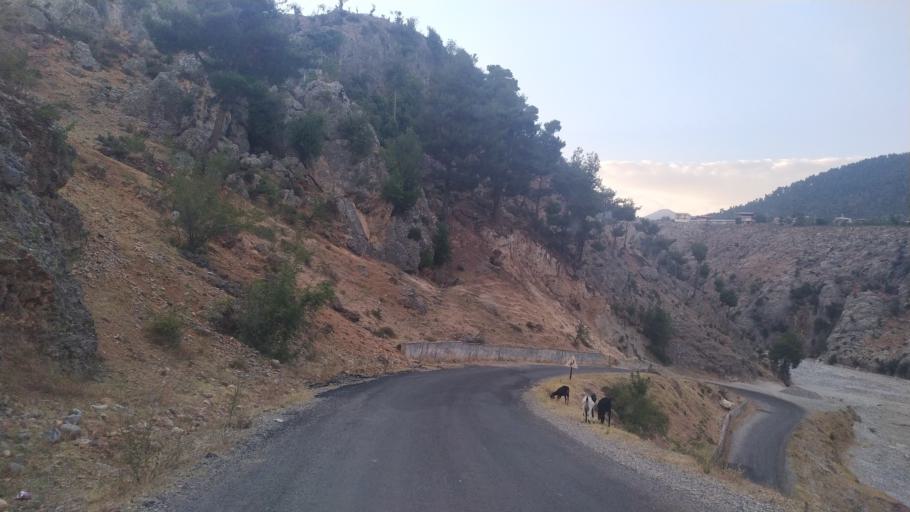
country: TR
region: Mersin
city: Camliyayla
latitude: 37.2392
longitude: 34.7133
